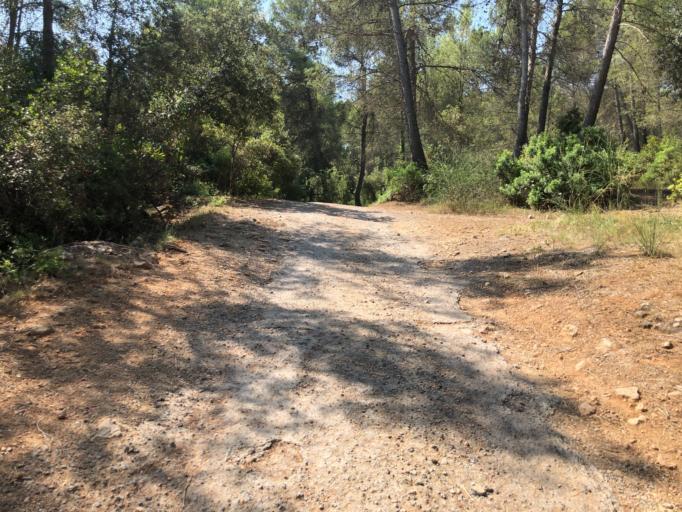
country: ES
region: Catalonia
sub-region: Provincia de Barcelona
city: Corbera de Llobregat
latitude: 41.4203
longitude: 1.9036
